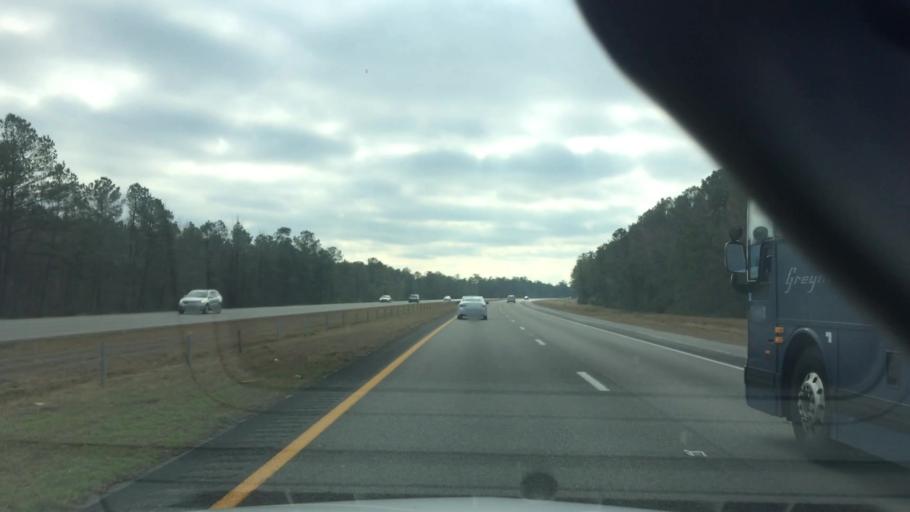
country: US
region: North Carolina
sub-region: New Hanover County
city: Castle Hayne
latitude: 34.3920
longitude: -77.8751
